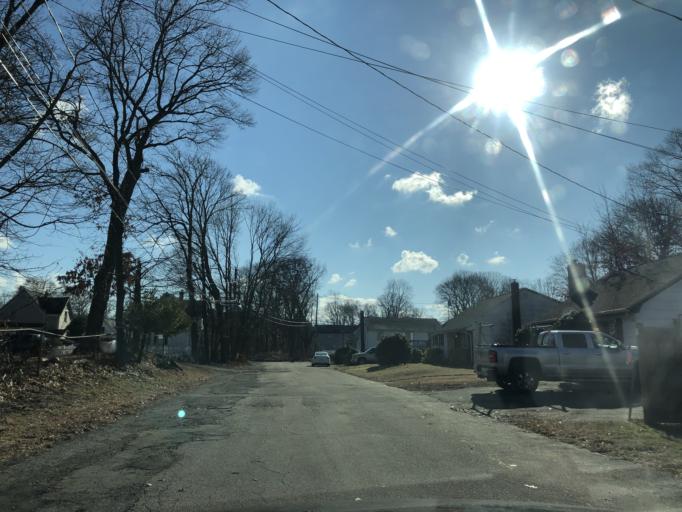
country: US
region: Massachusetts
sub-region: Plymouth County
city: Brockton
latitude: 42.1142
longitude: -71.0125
